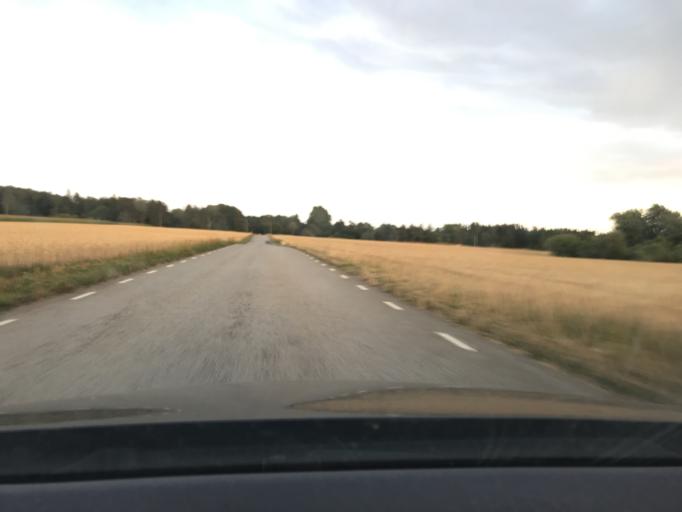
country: SE
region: Skane
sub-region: Simrishamns Kommun
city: Simrishamn
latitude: 55.4385
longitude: 14.2255
